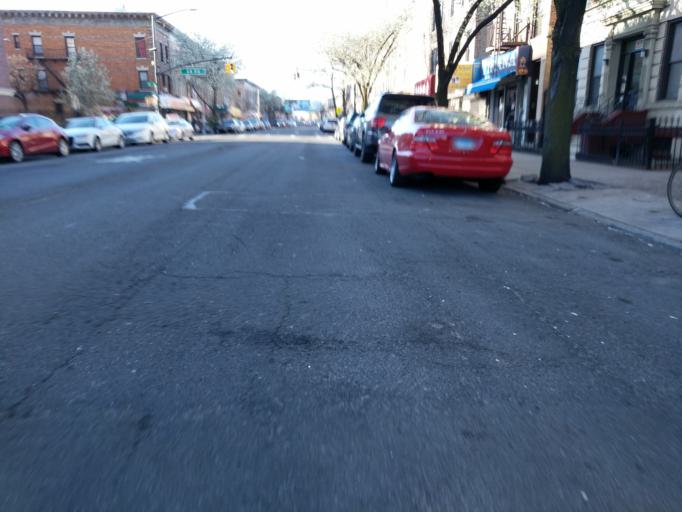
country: US
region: New York
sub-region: Kings County
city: East New York
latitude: 40.7041
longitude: -73.8957
